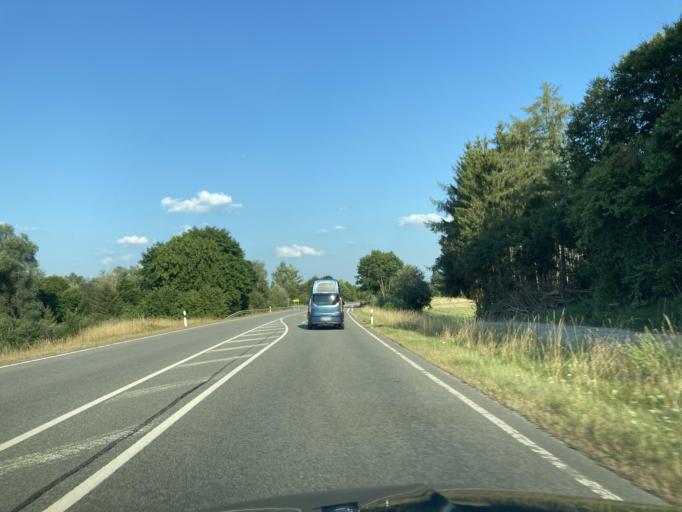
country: DE
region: Bavaria
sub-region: Upper Bavaria
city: Babensham
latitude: 48.0578
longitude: 12.2697
